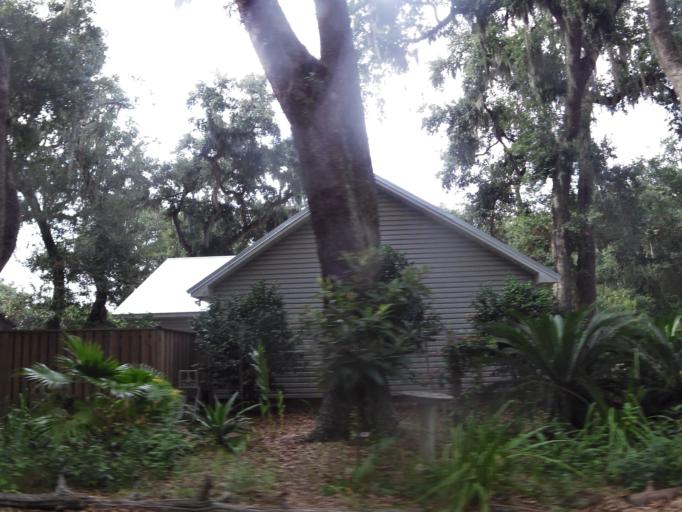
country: US
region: Georgia
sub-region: Glynn County
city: Saint Simons Island
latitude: 31.1393
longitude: -81.3964
